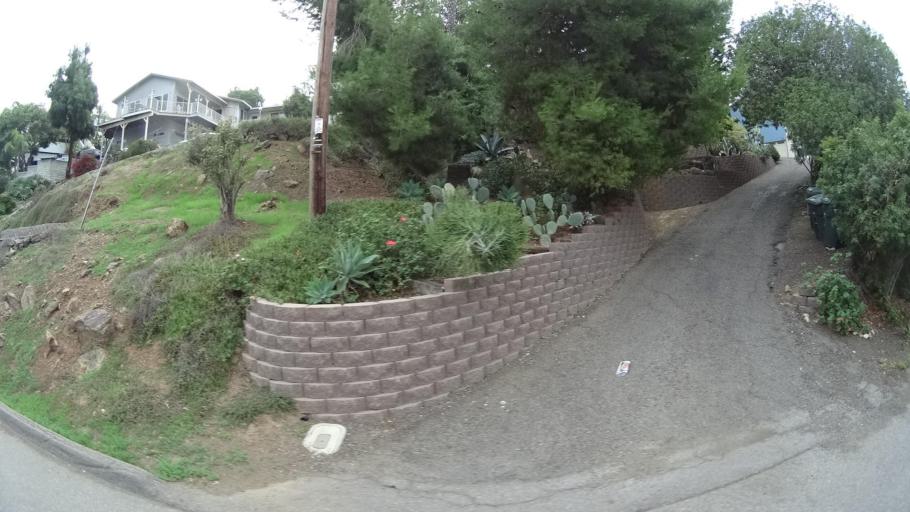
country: US
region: California
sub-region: San Diego County
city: Spring Valley
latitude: 32.7456
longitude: -117.0123
